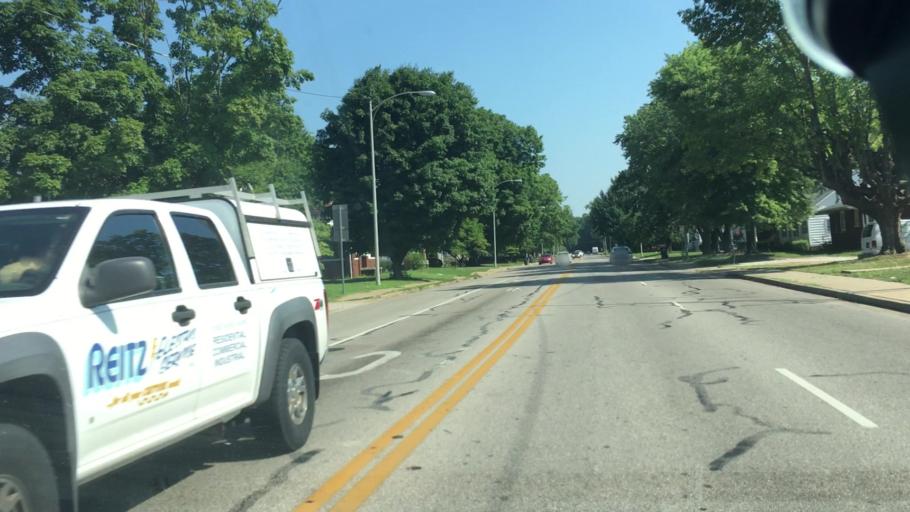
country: US
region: Indiana
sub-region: Vanderburgh County
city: Evansville
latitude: 37.9923
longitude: -87.5292
